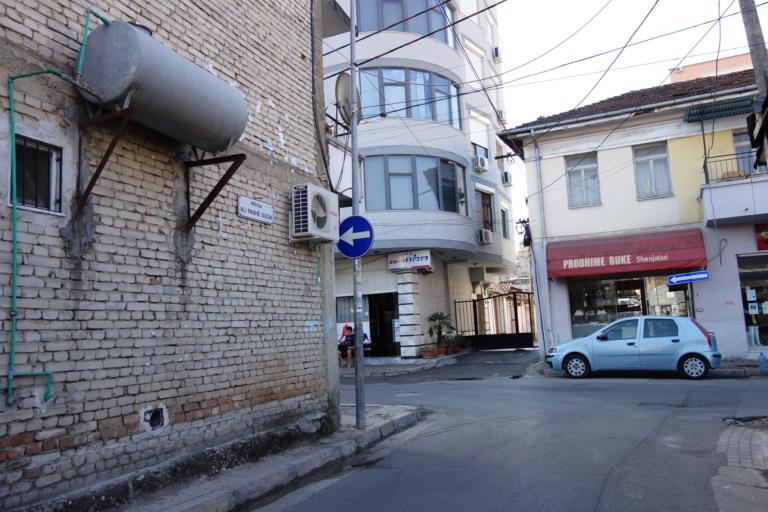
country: AL
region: Tirane
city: Tirana
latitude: 41.3321
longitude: 19.8266
